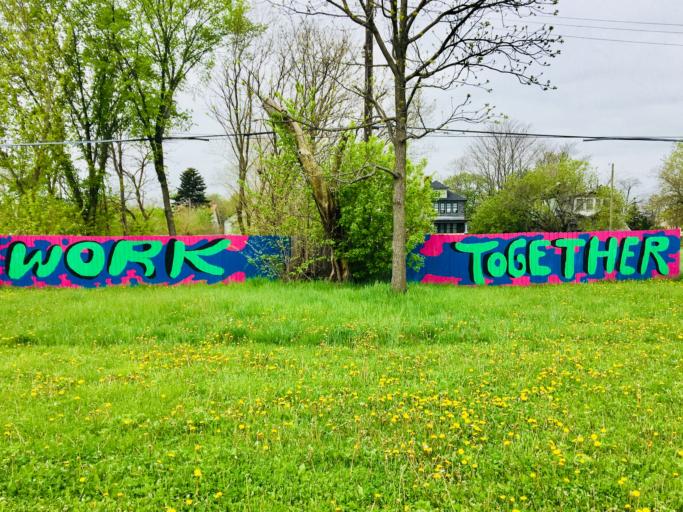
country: US
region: Michigan
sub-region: Wayne County
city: Grosse Pointe Park
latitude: 42.3763
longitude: -82.9583
